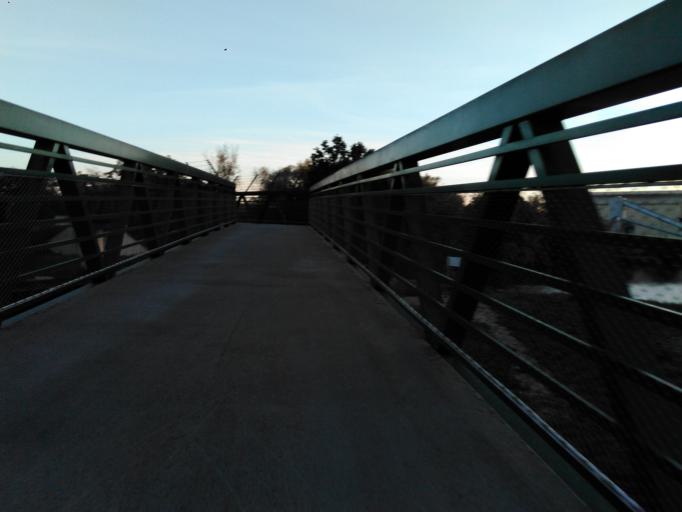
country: FR
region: Lorraine
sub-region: Departement de la Moselle
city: Saint-Julien-les-Metz
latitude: 49.1425
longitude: 6.1950
